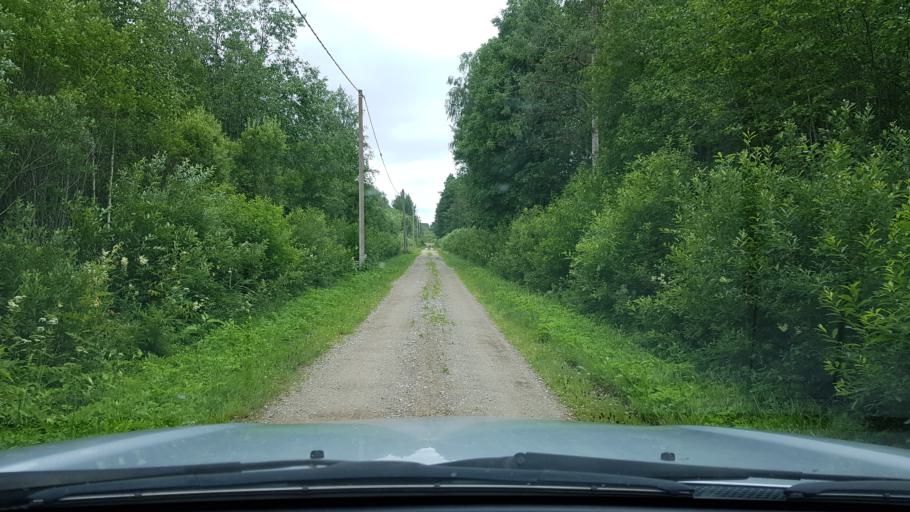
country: EE
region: Ida-Virumaa
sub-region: Narva-Joesuu linn
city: Narva-Joesuu
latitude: 59.3717
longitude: 28.0528
